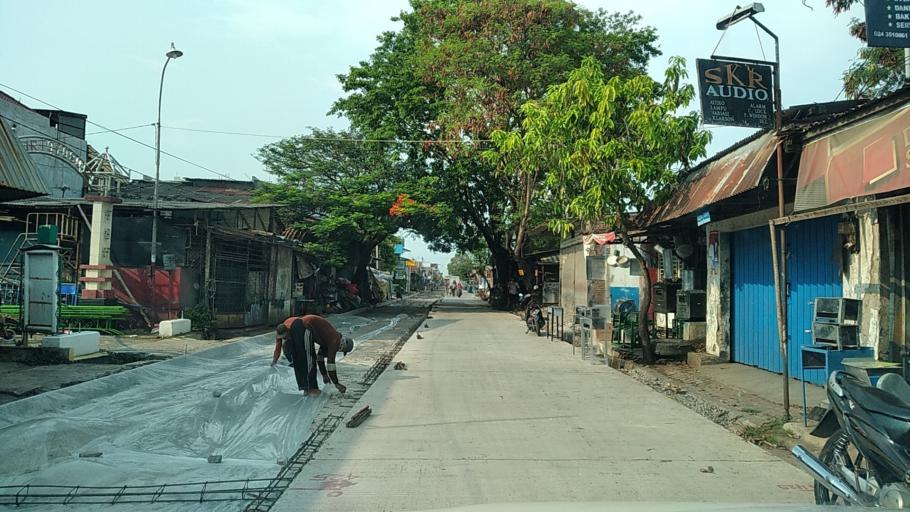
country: ID
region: Central Java
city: Semarang
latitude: -6.9773
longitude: 110.4414
